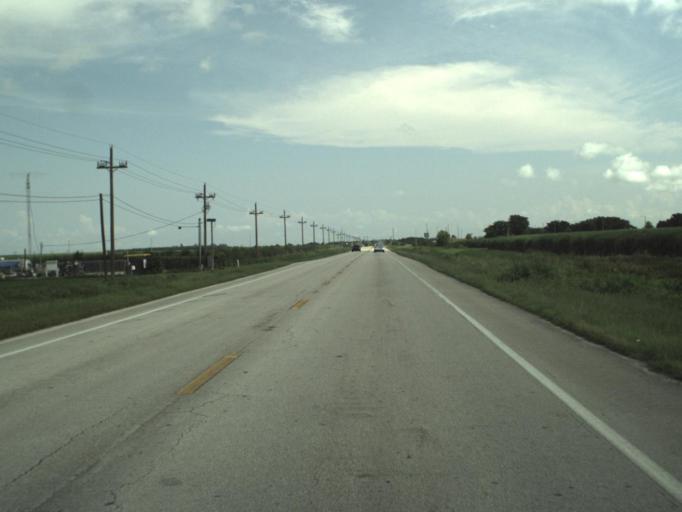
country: US
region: Florida
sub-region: Palm Beach County
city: Belle Glade
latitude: 26.7141
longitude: -80.6840
